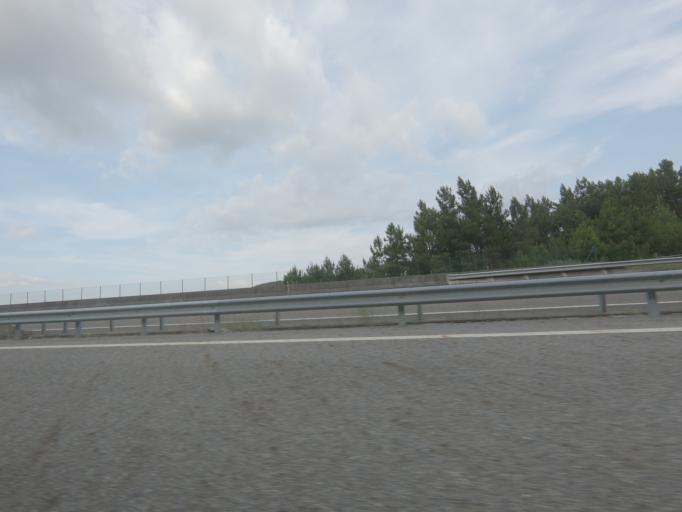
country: PT
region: Vila Real
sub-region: Boticas
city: Boticas
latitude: 41.6868
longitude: -7.5624
